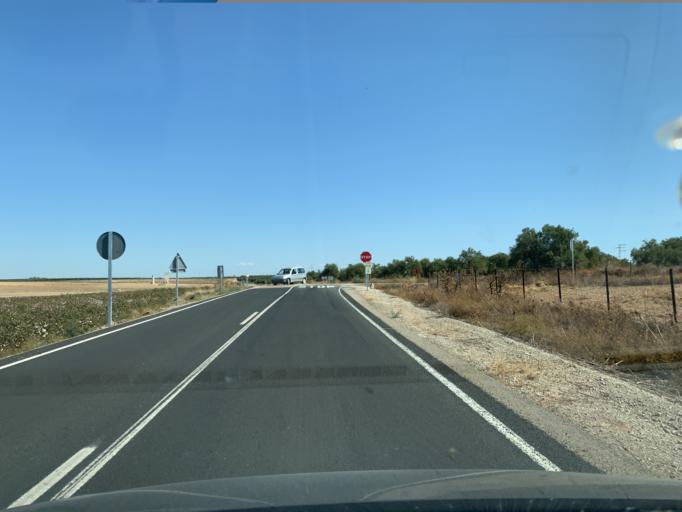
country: ES
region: Andalusia
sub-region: Provincia de Sevilla
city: La Lantejuela
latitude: 37.3382
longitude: -5.2875
